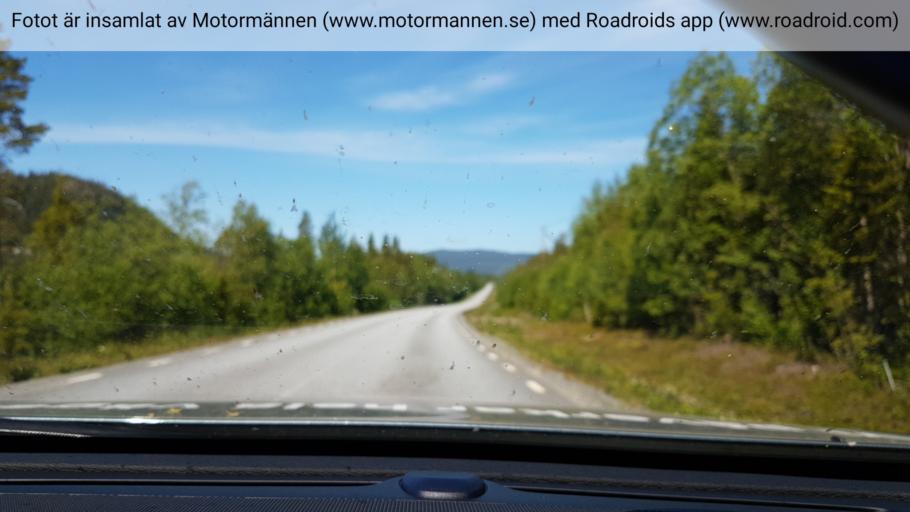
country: SE
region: Vaesterbotten
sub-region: Vilhelmina Kommun
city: Sjoberg
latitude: 64.6719
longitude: 15.5918
